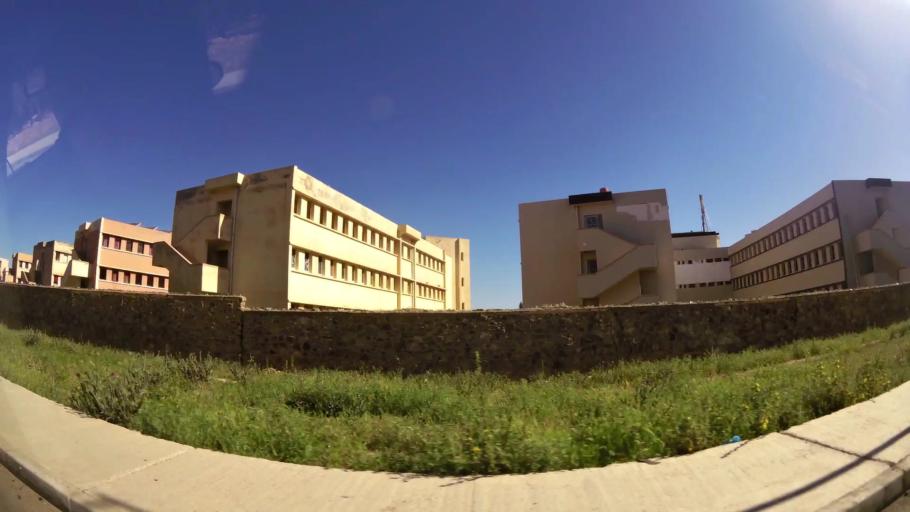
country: MA
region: Oriental
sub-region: Oujda-Angad
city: Oujda
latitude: 34.6480
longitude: -1.8977
